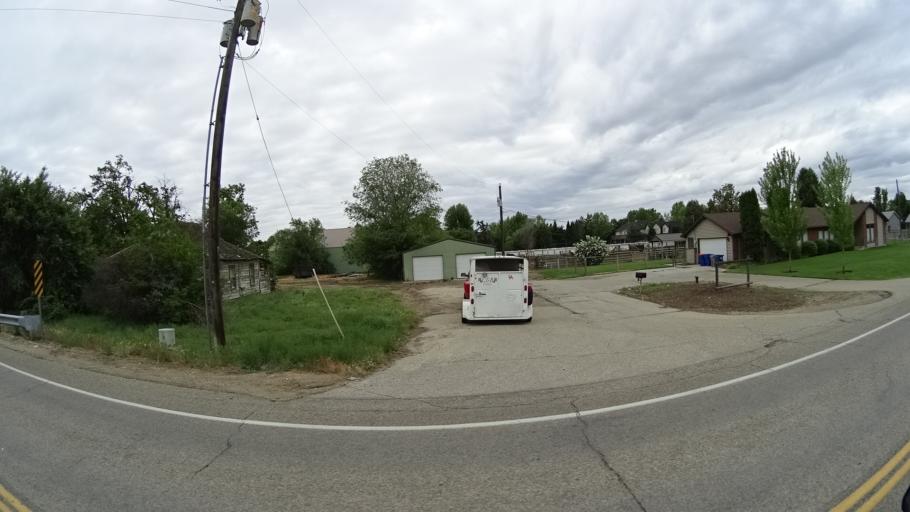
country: US
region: Idaho
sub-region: Ada County
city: Eagle
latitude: 43.7063
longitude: -116.3883
